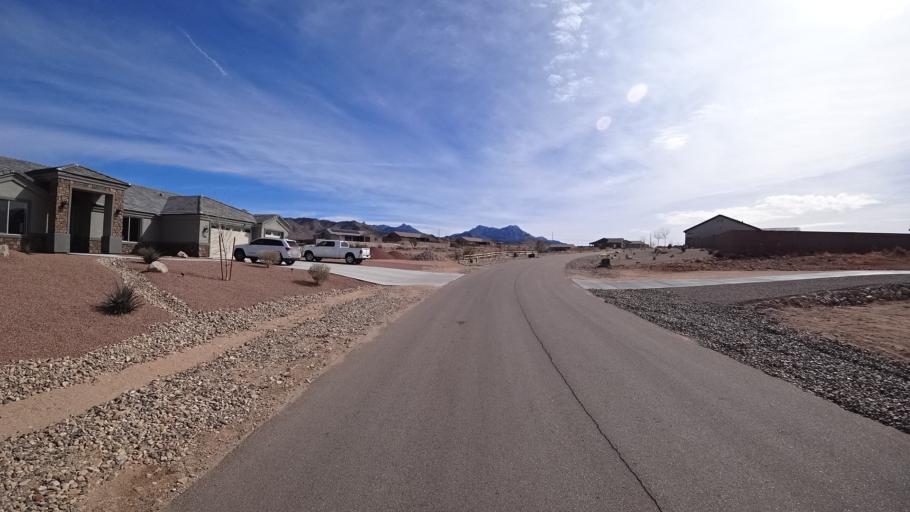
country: US
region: Arizona
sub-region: Mohave County
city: Kingman
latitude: 35.1846
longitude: -113.9783
